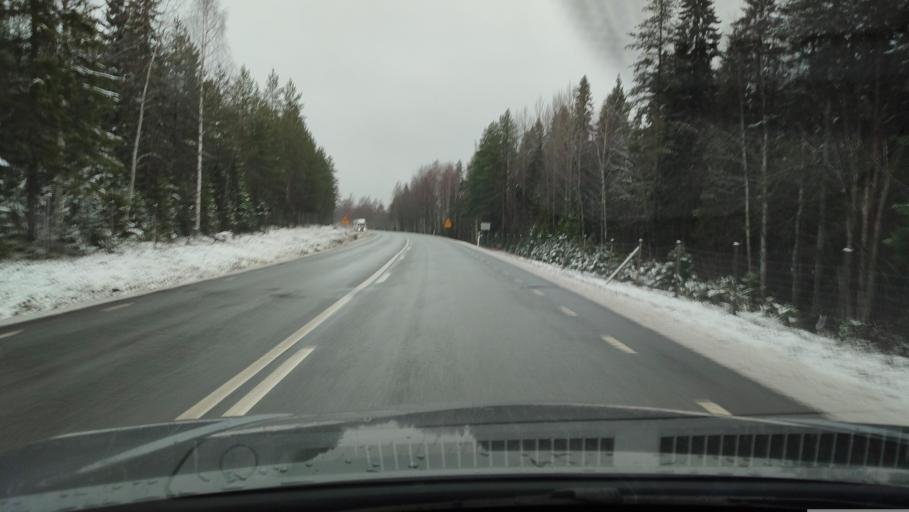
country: SE
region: Vaesterbotten
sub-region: Skelleftea Kommun
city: Burea
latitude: 64.5349
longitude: 21.2588
